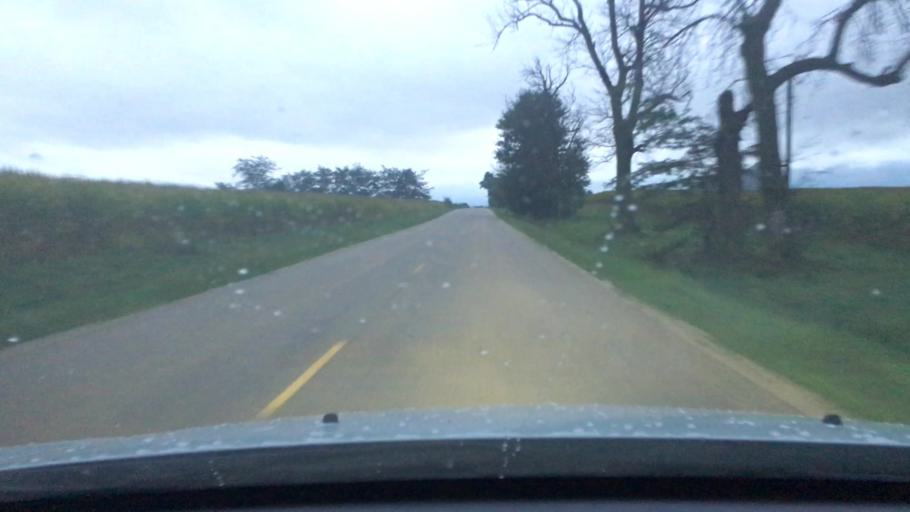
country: US
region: Illinois
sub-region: DeKalb County
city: Malta
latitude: 41.8797
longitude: -88.9616
